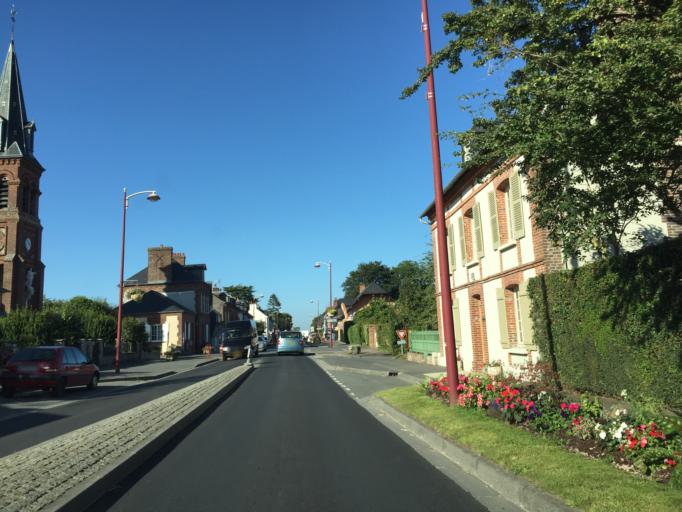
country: FR
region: Lower Normandy
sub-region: Departement du Calvados
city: Equemauville
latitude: 49.3919
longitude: 0.2072
